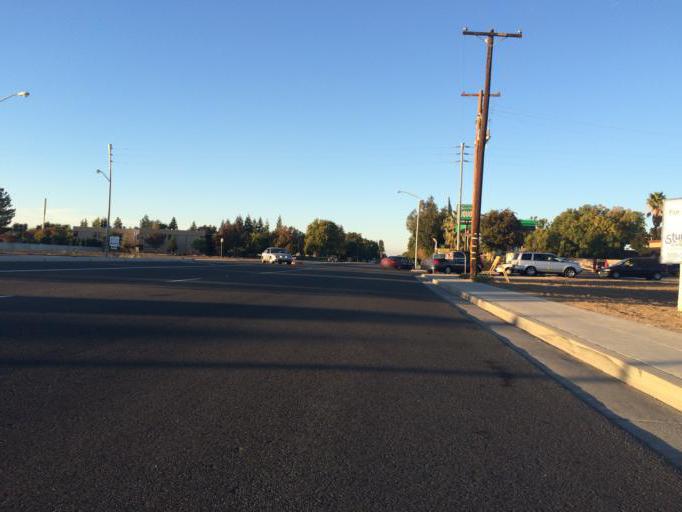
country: US
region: California
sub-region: Fresno County
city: Tarpey Village
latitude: 36.7973
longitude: -119.7273
